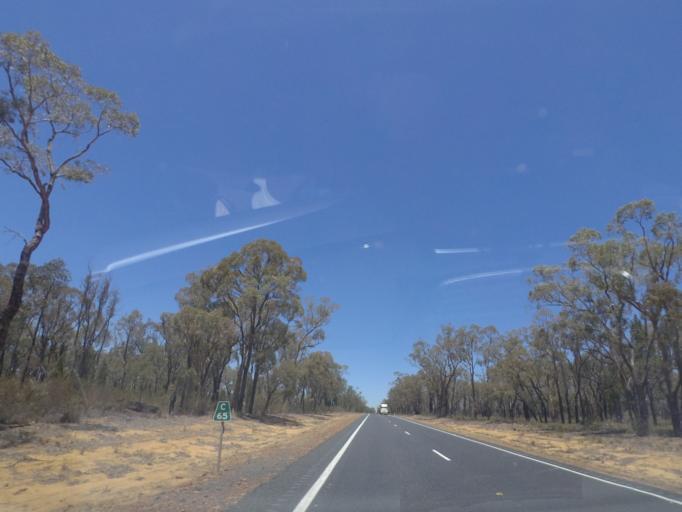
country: AU
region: New South Wales
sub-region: Narrabri
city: Narrabri
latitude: -30.7429
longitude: 149.5145
